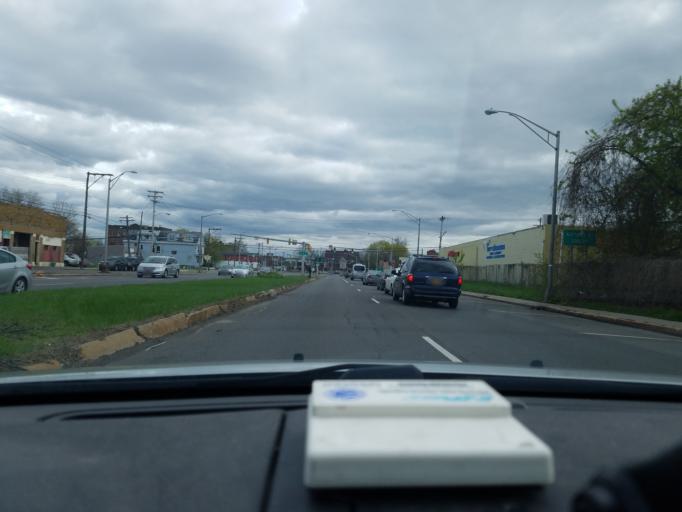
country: US
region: New York
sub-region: Onondaga County
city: Syracuse
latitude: 43.0444
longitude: -76.1584
